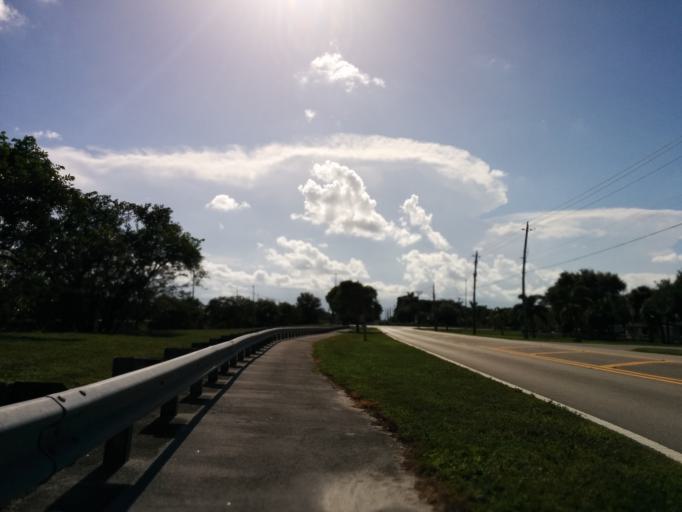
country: US
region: Florida
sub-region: Broward County
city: Davie
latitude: 26.0653
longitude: -80.2502
